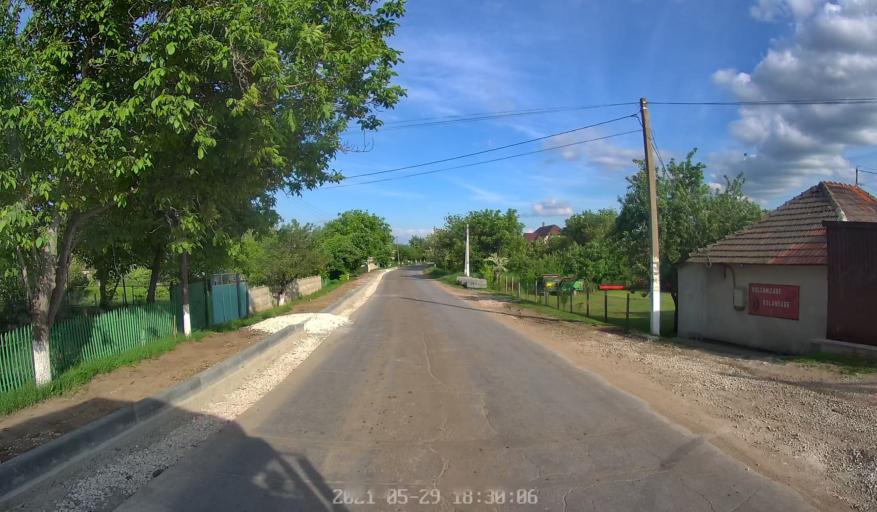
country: MD
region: Chisinau
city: Singera
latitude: 46.8239
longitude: 28.8761
